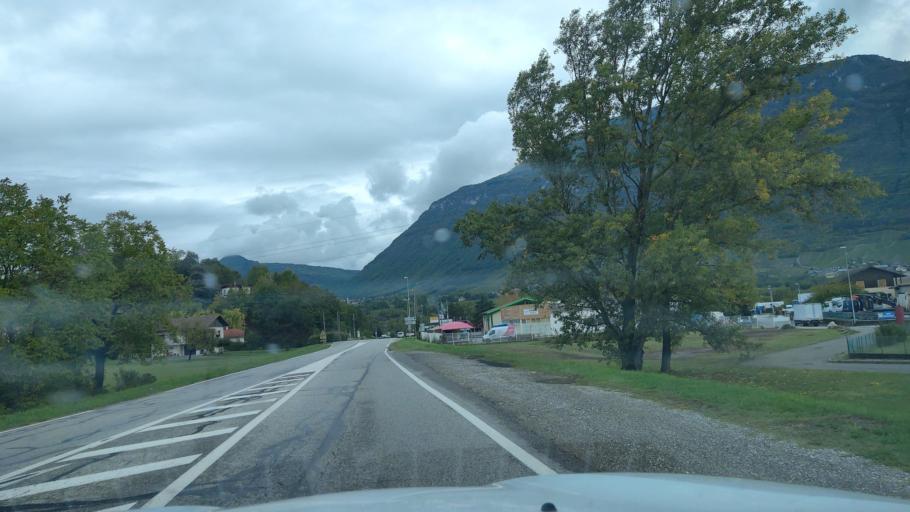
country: FR
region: Rhone-Alpes
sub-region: Departement de la Savoie
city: Les Marches
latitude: 45.5059
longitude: 6.0028
